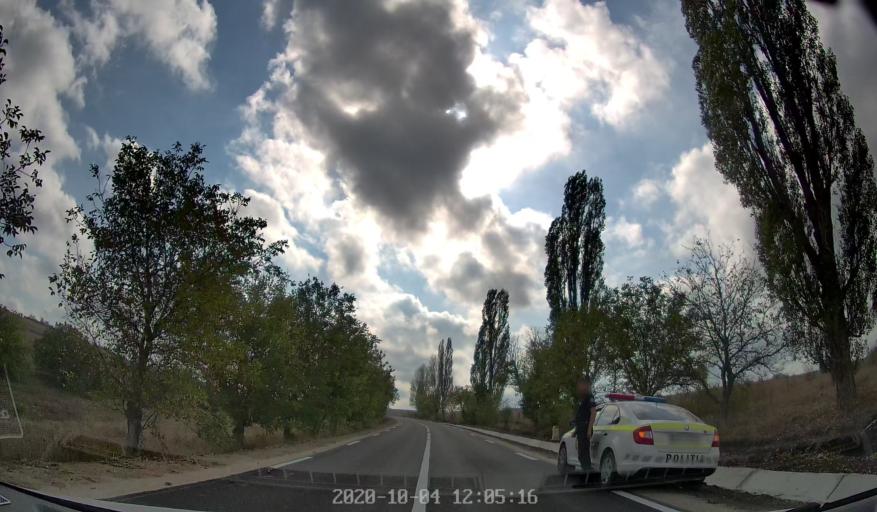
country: MD
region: Rezina
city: Saharna
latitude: 47.5955
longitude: 28.9495
